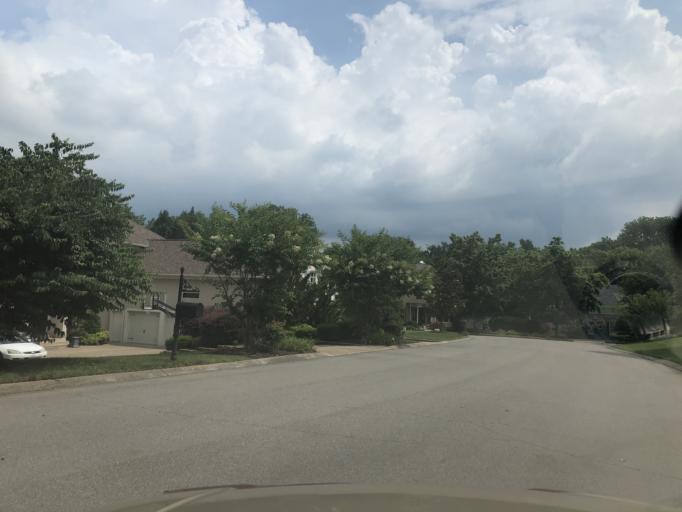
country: US
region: Tennessee
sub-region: Davidson County
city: Lakewood
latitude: 36.2354
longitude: -86.6029
